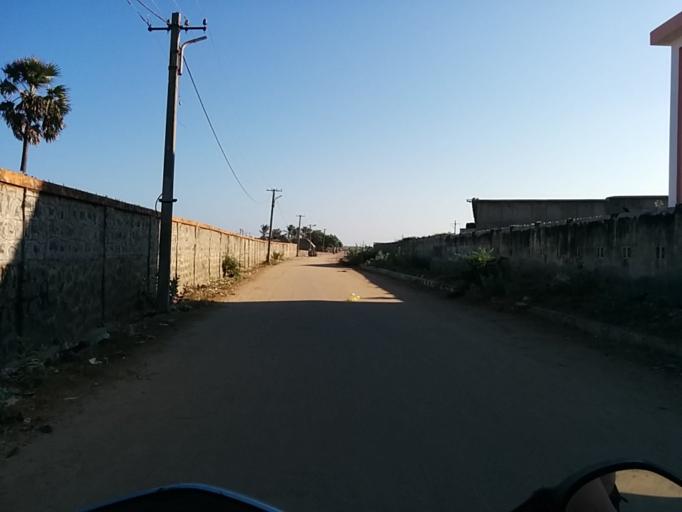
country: IN
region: Pondicherry
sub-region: Puducherry
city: Puducherry
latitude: 11.9163
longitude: 79.8305
